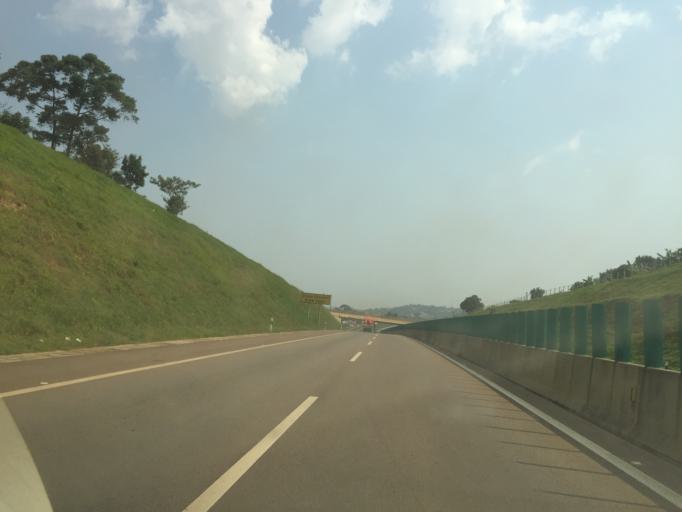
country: UG
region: Central Region
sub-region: Wakiso District
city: Kajansi
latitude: 0.2800
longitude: 32.5143
